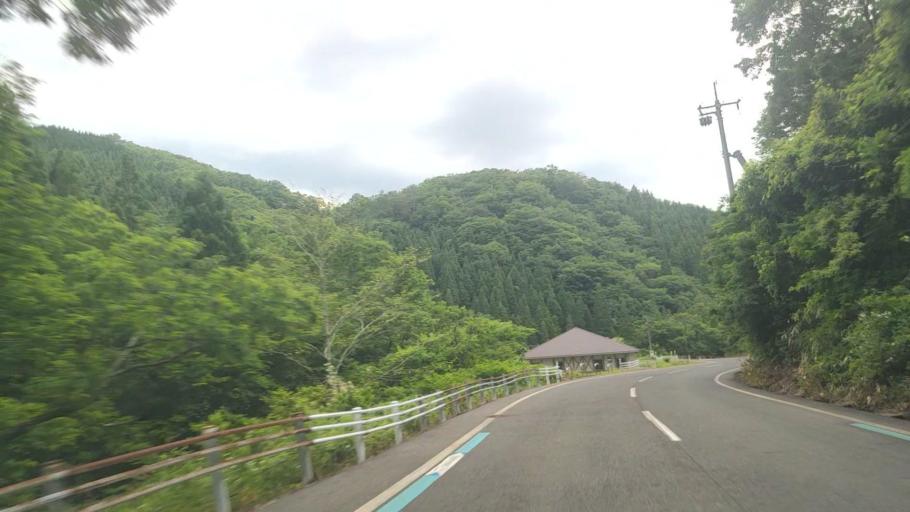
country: JP
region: Tottori
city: Kurayoshi
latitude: 35.2904
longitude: 133.9899
